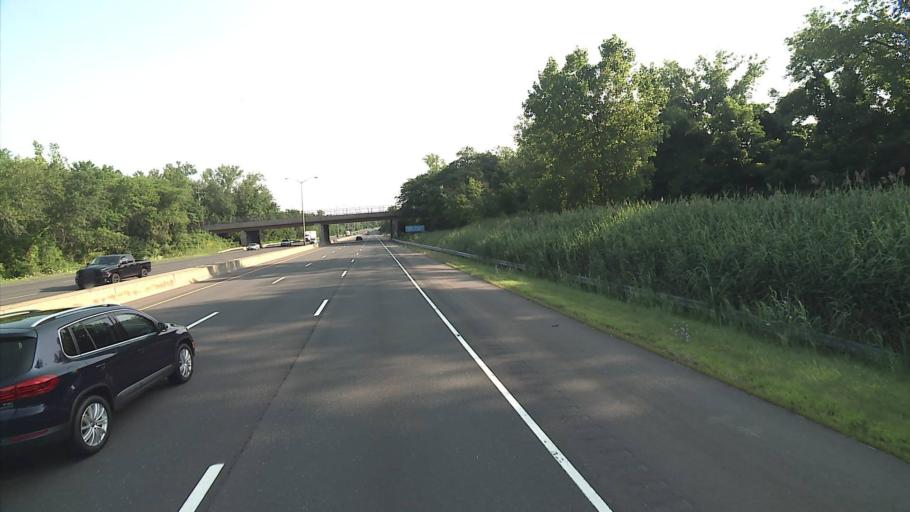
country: US
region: Connecticut
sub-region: Hartford County
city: Windsor Locks
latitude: 41.9422
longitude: -72.6063
